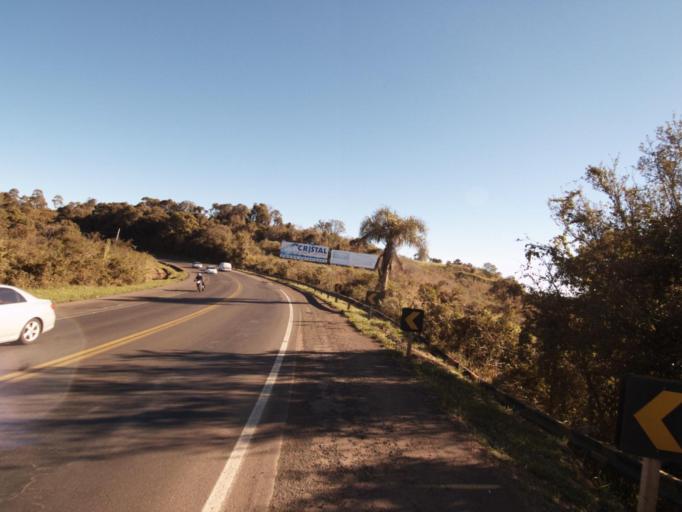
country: BR
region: Santa Catarina
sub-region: Chapeco
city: Chapeco
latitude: -26.9744
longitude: -52.5876
